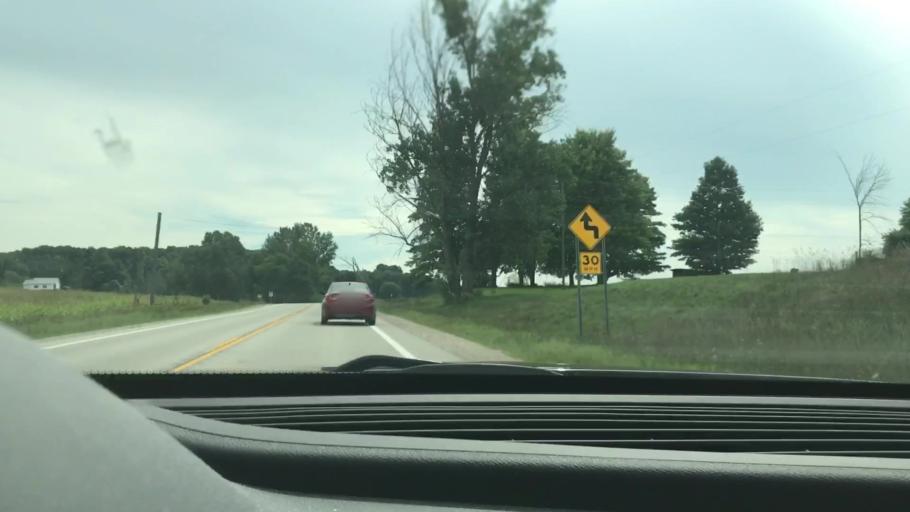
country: US
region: Michigan
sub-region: Antrim County
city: Bellaire
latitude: 45.0879
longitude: -85.2899
